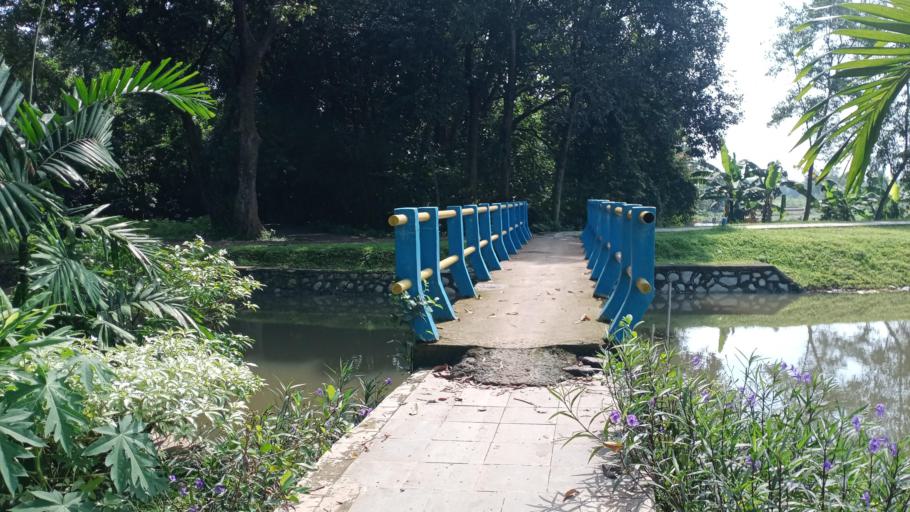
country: ID
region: West Java
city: Cileungsir
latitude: -6.3947
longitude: 107.0860
